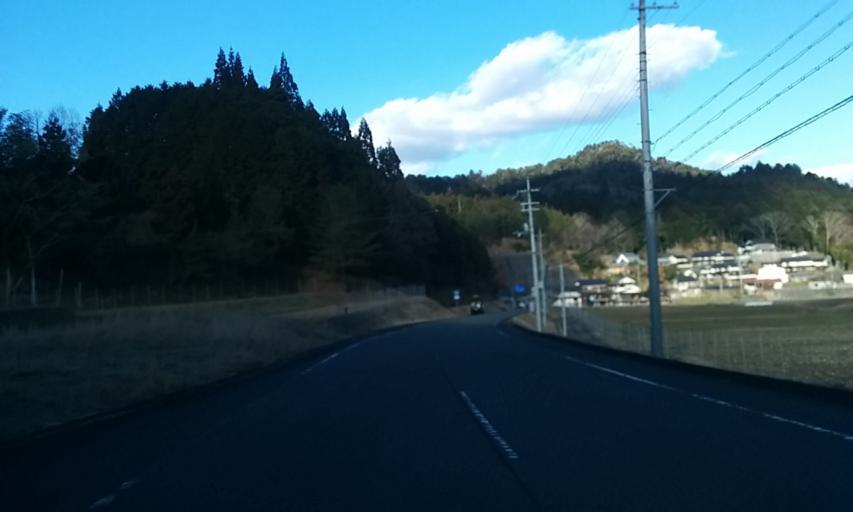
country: JP
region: Kyoto
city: Fukuchiyama
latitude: 35.2803
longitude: 135.0338
